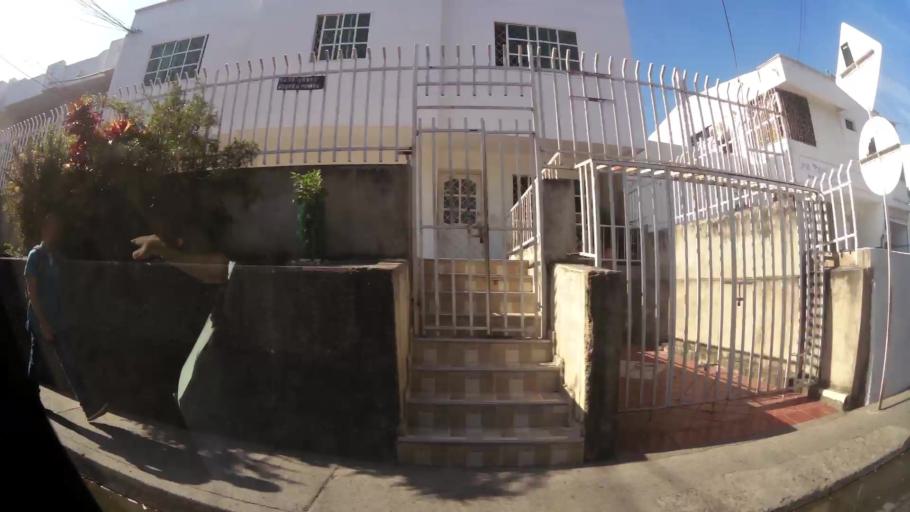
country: CO
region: Bolivar
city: Cartagena
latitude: 10.3934
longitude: -75.4892
